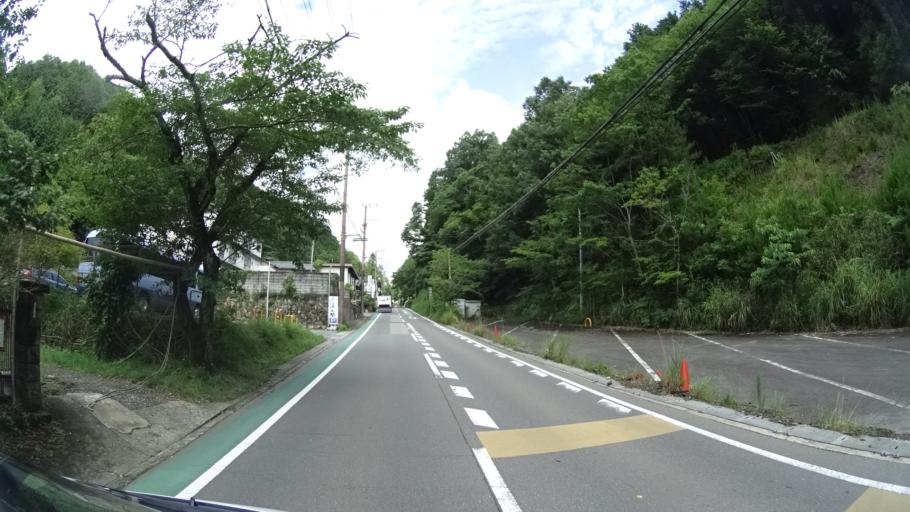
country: JP
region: Kyoto
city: Kameoka
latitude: 35.0185
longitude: 135.5191
